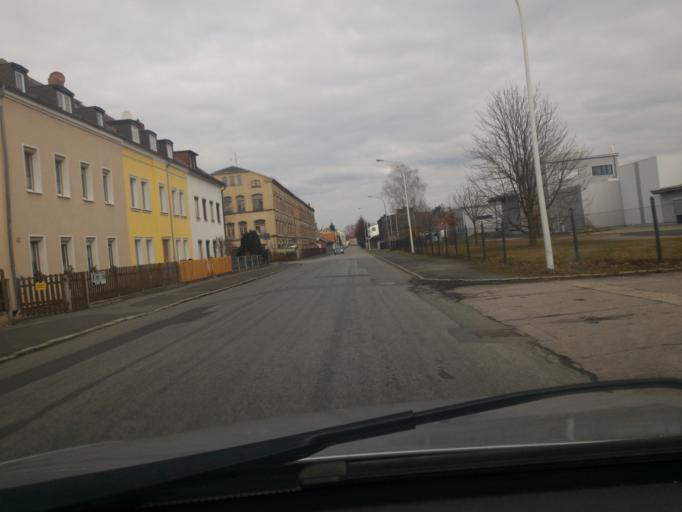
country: DE
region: Saxony
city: Zittau
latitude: 50.8808
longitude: 14.8129
